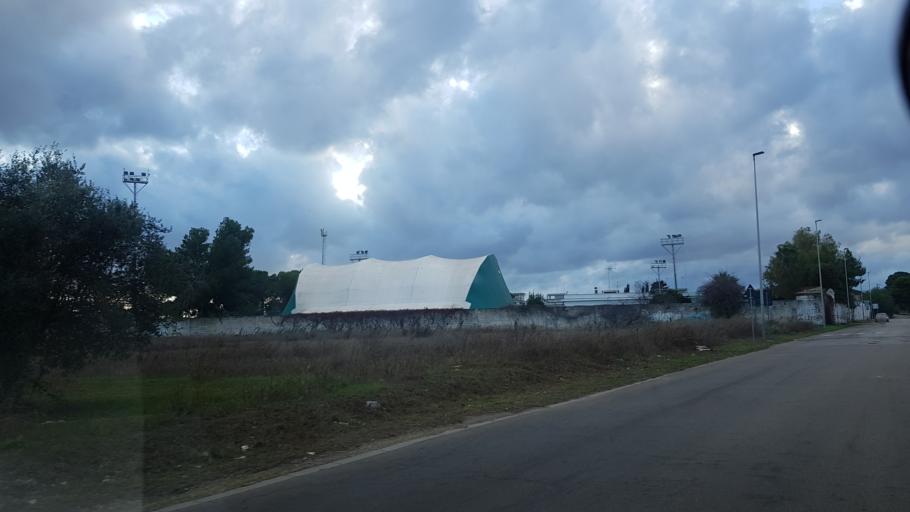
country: IT
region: Apulia
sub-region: Provincia di Brindisi
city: San Pietro Vernotico
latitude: 40.4878
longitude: 18.0069
